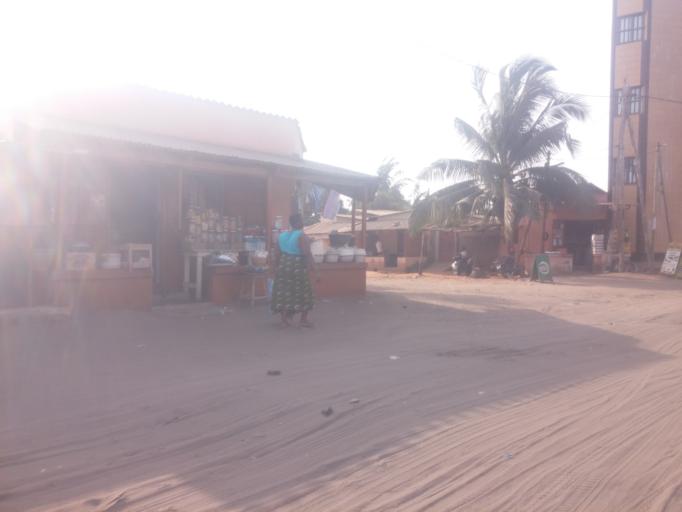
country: TG
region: Maritime
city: Lome
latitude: 6.1695
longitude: 1.2769
